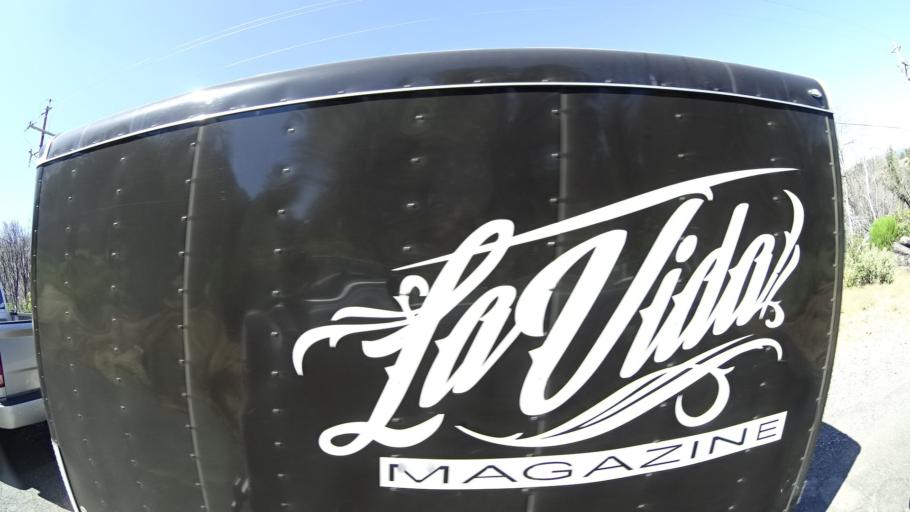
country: US
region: California
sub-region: Calaveras County
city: Mountain Ranch
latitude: 38.2879
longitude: -120.5886
